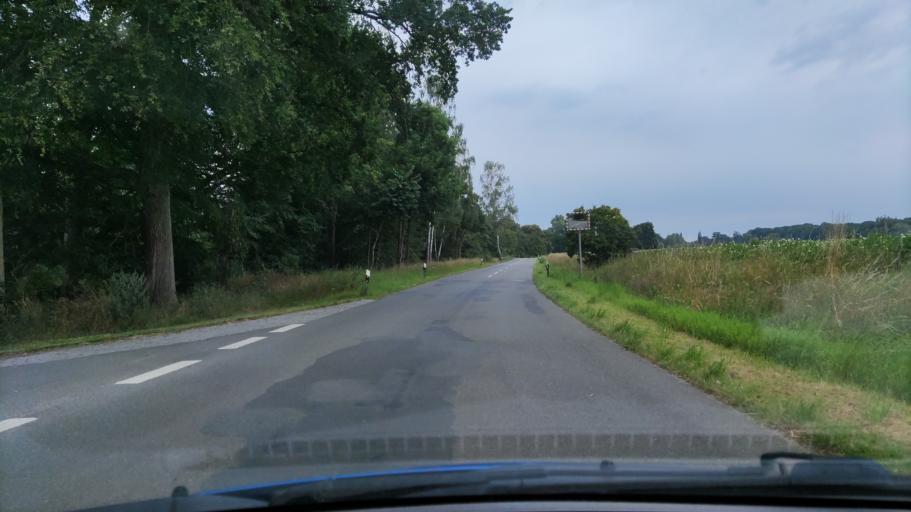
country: DE
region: Lower Saxony
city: Suhlendorf
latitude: 52.9668
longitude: 10.8070
